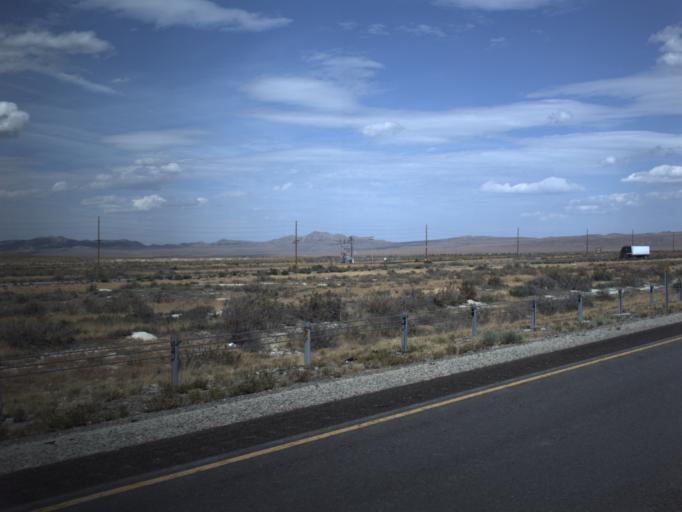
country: US
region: Utah
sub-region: Tooele County
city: Grantsville
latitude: 40.7281
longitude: -113.1259
